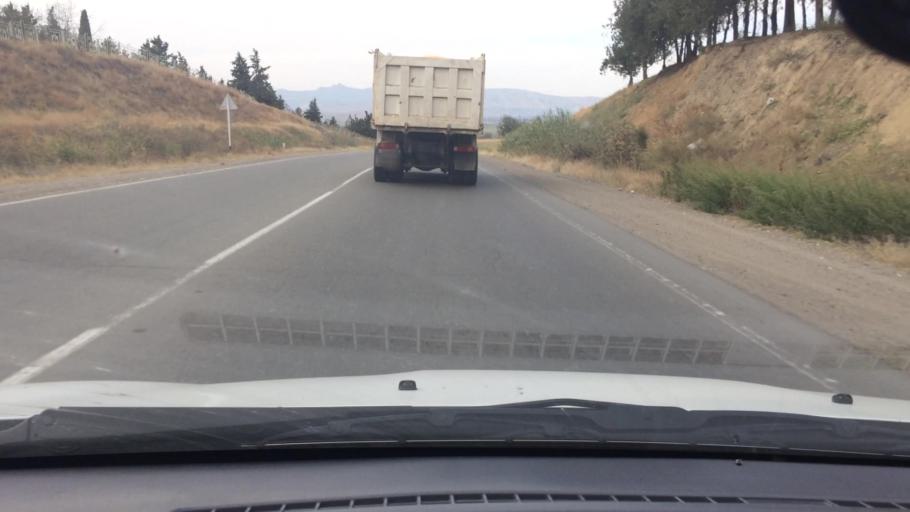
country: GE
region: Kvemo Kartli
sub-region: Marneuli
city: Marneuli
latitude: 41.5231
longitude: 44.7785
